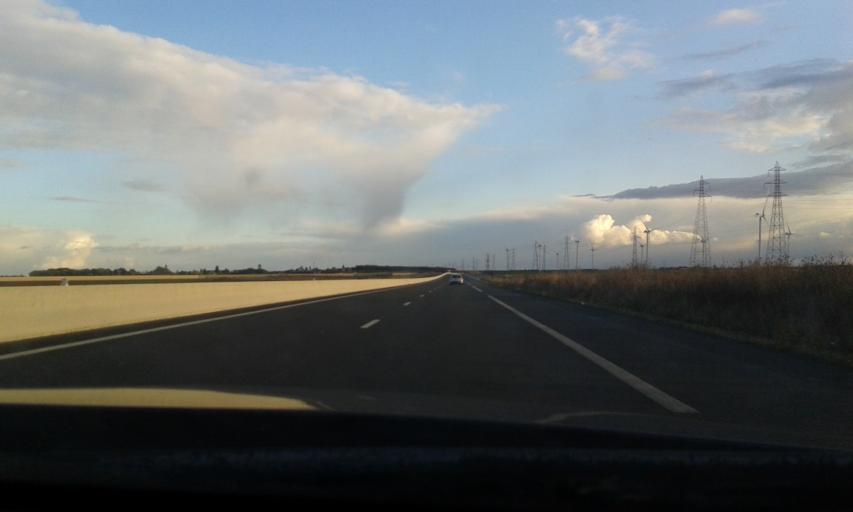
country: FR
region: Centre
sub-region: Departement d'Eure-et-Loir
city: Voves
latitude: 48.3387
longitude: 1.6378
